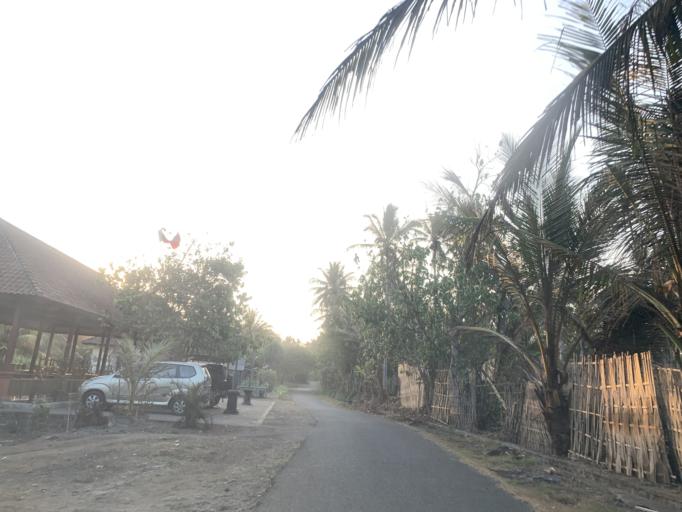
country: ID
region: Bali
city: Banjar Swastika
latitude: -8.4374
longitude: 114.8512
